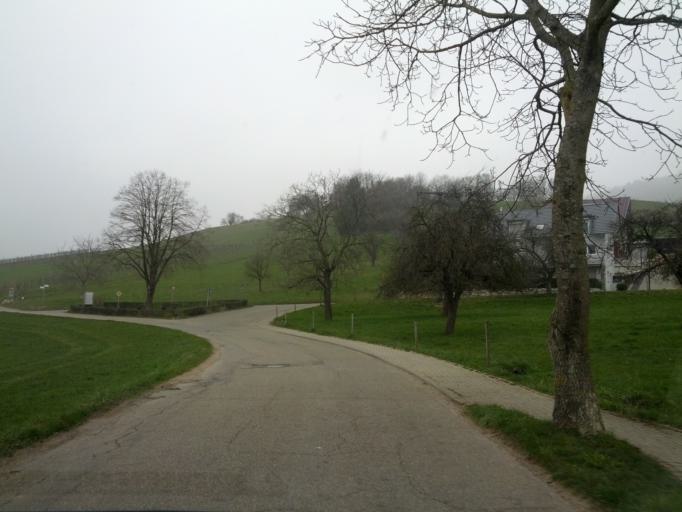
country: DE
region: Baden-Wuerttemberg
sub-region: Freiburg Region
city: Wittnau
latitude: 47.9427
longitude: 7.8108
